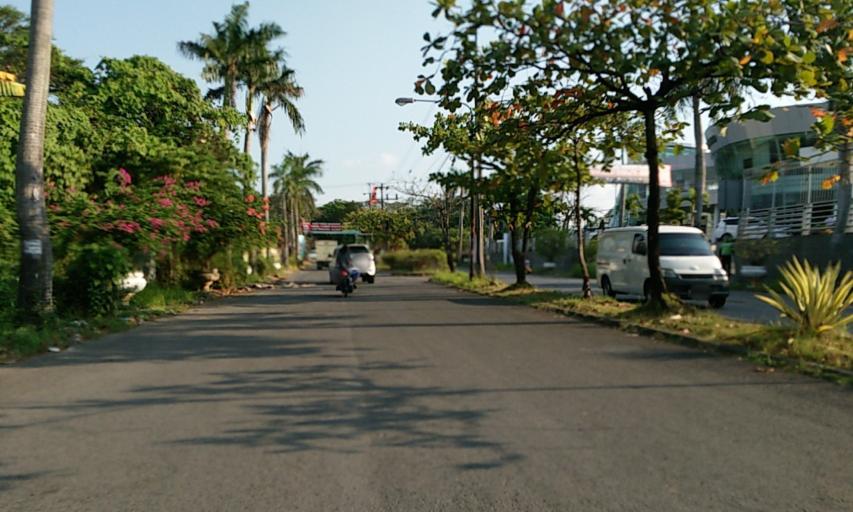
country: ID
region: Central Java
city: Mranggen
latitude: -7.0136
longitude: 110.4822
